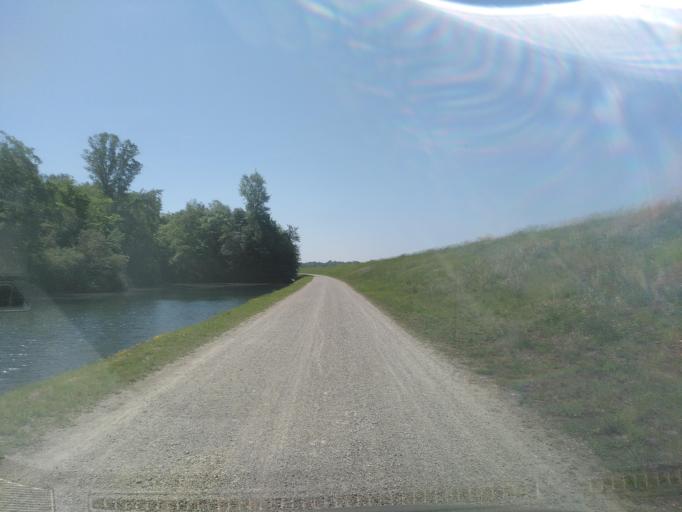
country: FR
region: Alsace
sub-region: Departement du Haut-Rhin
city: Kunheim
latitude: 48.0879
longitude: 7.5734
